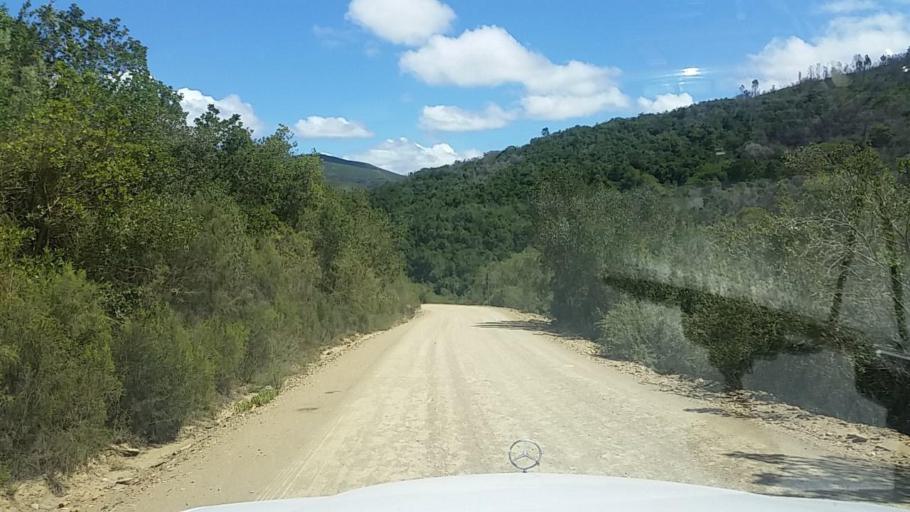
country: ZA
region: Western Cape
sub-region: Eden District Municipality
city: Knysna
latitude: -33.8581
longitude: 23.1811
